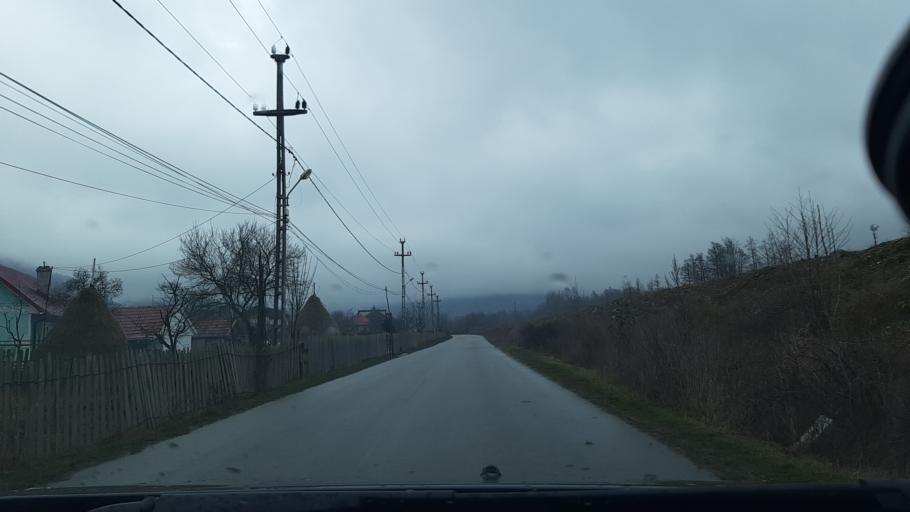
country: RO
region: Hunedoara
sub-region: Oras Petrila
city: Petrila
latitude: 45.4328
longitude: 23.4197
